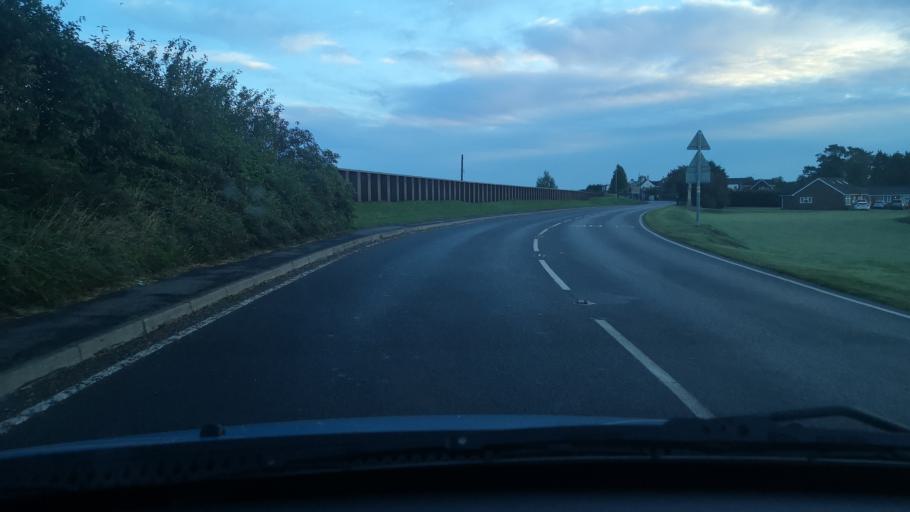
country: GB
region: England
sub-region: East Riding of Yorkshire
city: Skelton
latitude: 53.6873
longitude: -0.8424
